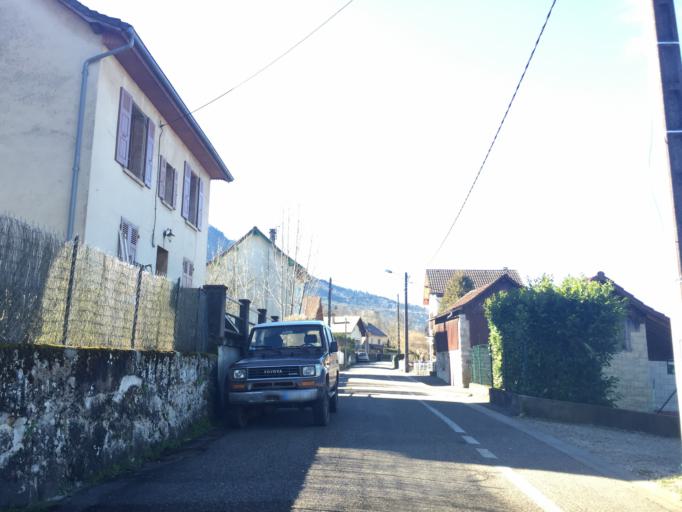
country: FR
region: Rhone-Alpes
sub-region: Departement de l'Isere
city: Saint-Laurent-du-Pont
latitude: 45.3909
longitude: 5.7442
